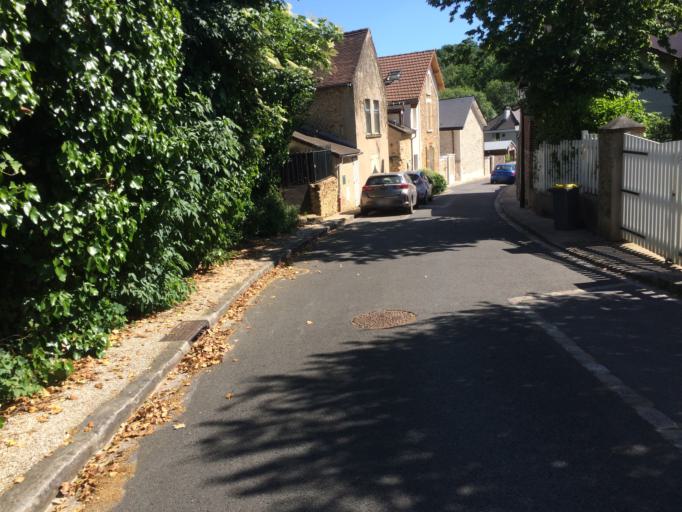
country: FR
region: Ile-de-France
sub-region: Departement de l'Essonne
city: Vauhallan
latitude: 48.7331
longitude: 2.2066
